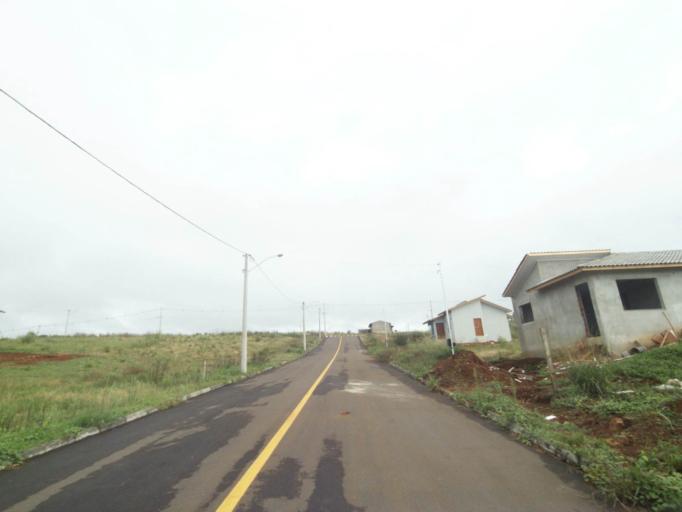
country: BR
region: Rio Grande do Sul
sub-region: Lagoa Vermelha
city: Lagoa Vermelha
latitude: -28.2291
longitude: -51.5207
